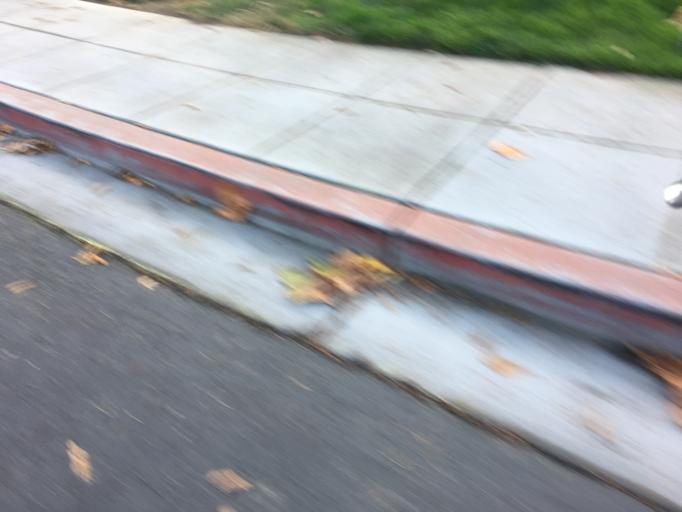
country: US
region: California
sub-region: San Mateo County
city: Menlo Park
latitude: 37.4524
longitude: -122.1667
